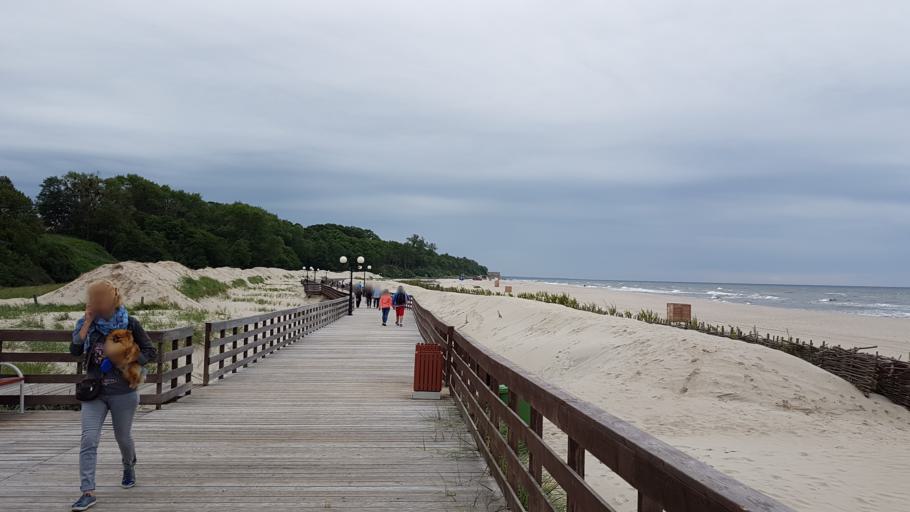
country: RU
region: Kaliningrad
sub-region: Gorod Kaliningrad
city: Yantarnyy
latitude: 54.8742
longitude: 19.9329
